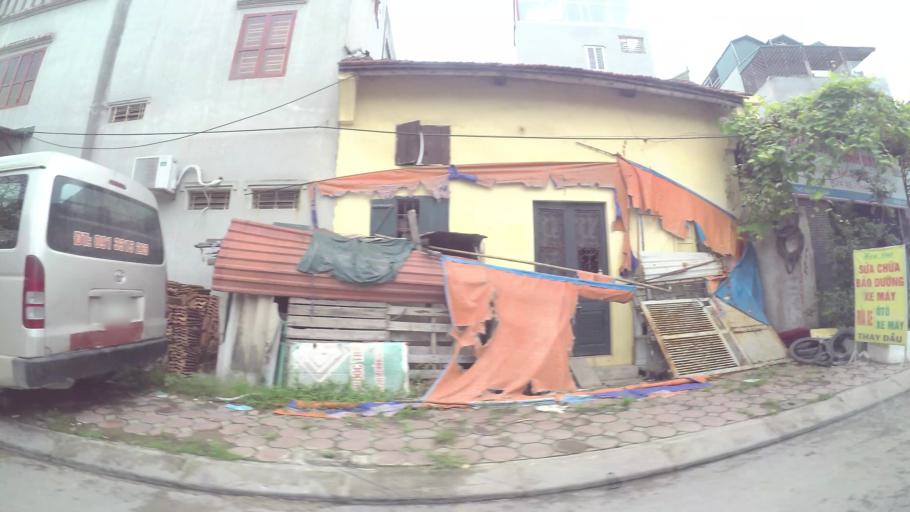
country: VN
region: Ha Noi
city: Van Dien
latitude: 20.9763
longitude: 105.8495
